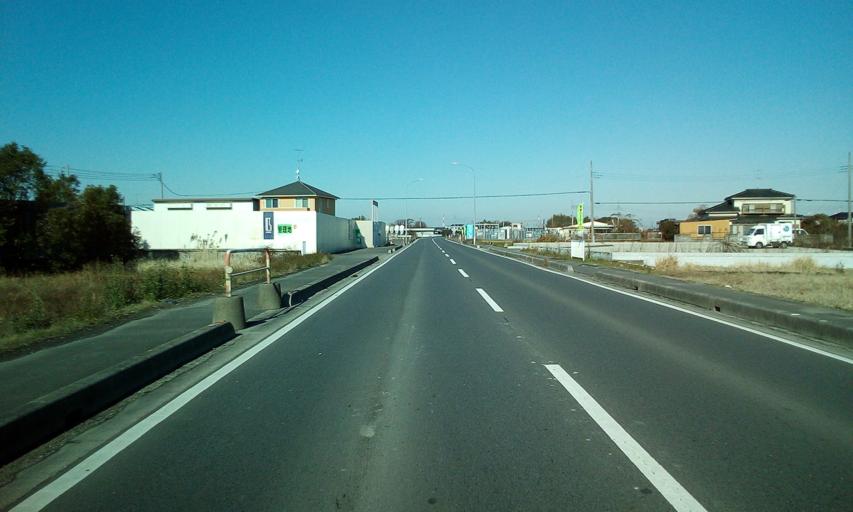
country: JP
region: Chiba
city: Nagareyama
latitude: 35.8753
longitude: 139.8891
